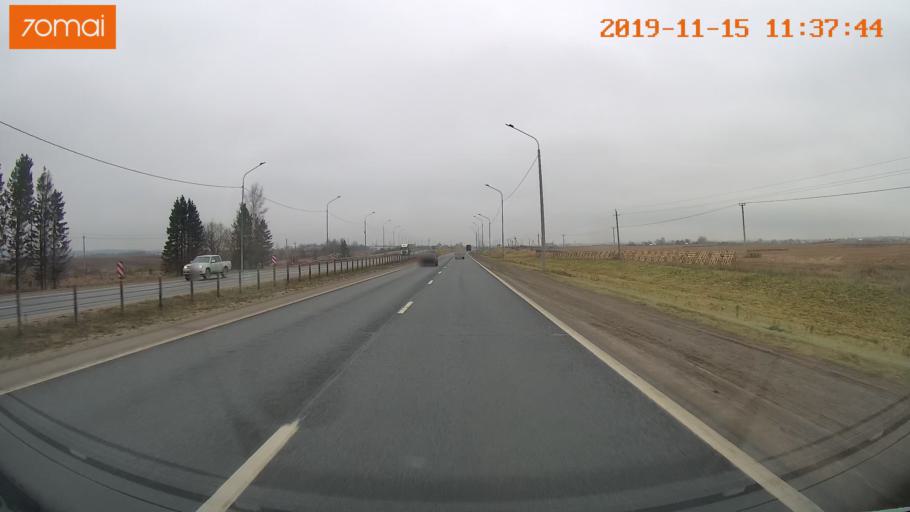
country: RU
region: Vologda
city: Molochnoye
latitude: 59.2069
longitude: 39.6795
